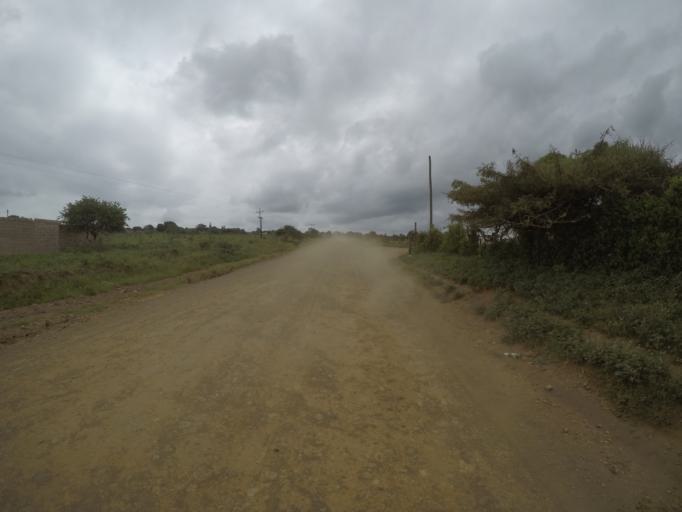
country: ZA
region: KwaZulu-Natal
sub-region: uThungulu District Municipality
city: Empangeni
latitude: -28.5850
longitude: 31.8454
